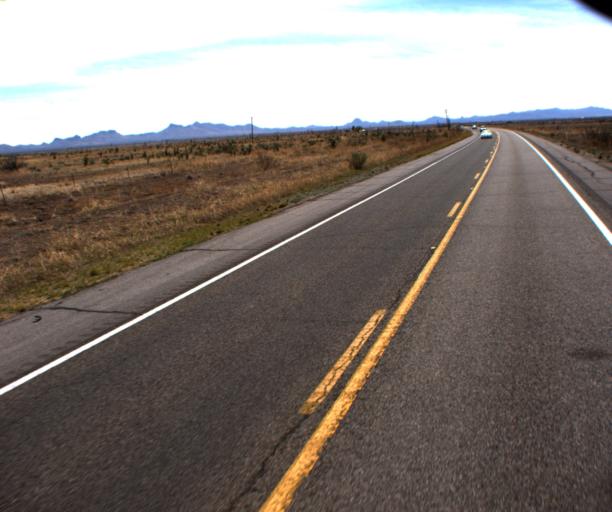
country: US
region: Arizona
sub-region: Cochise County
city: Pirtleville
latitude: 31.4548
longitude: -109.6097
